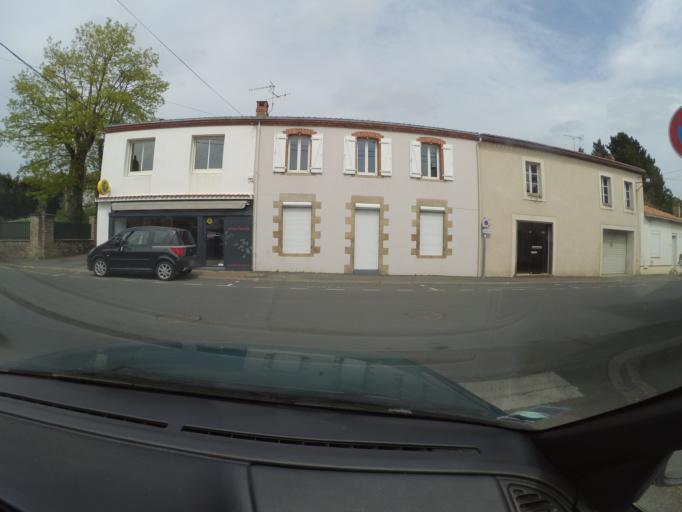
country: FR
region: Pays de la Loire
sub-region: Departement de la Loire-Atlantique
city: Clisson
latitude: 47.0900
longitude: -1.2870
